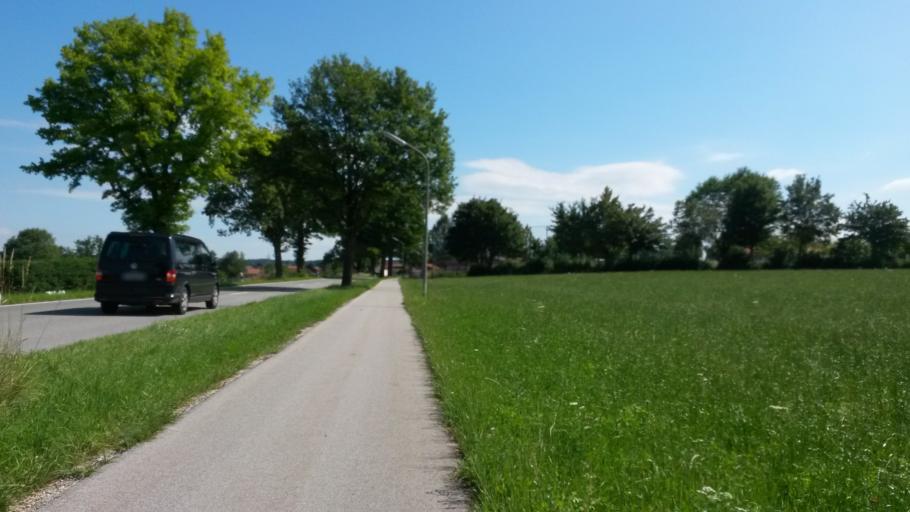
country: DE
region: Bavaria
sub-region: Upper Bavaria
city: Grabenstatt
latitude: 47.8390
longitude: 12.5366
